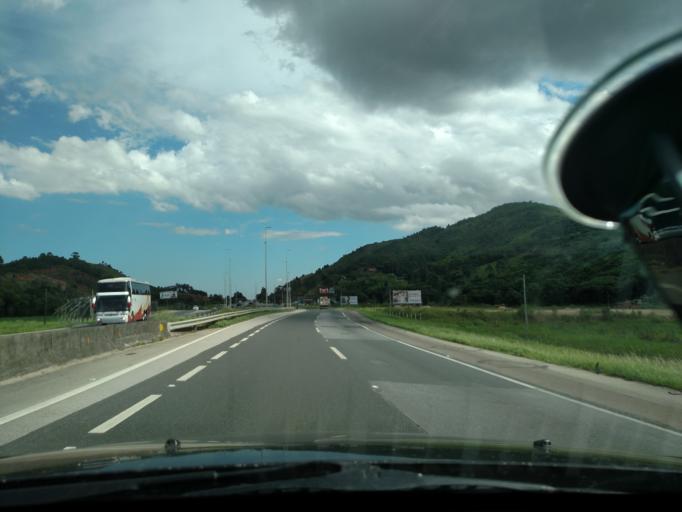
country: BR
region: Santa Catarina
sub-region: Tijucas
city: Tijucas
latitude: -27.2773
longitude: -48.6314
